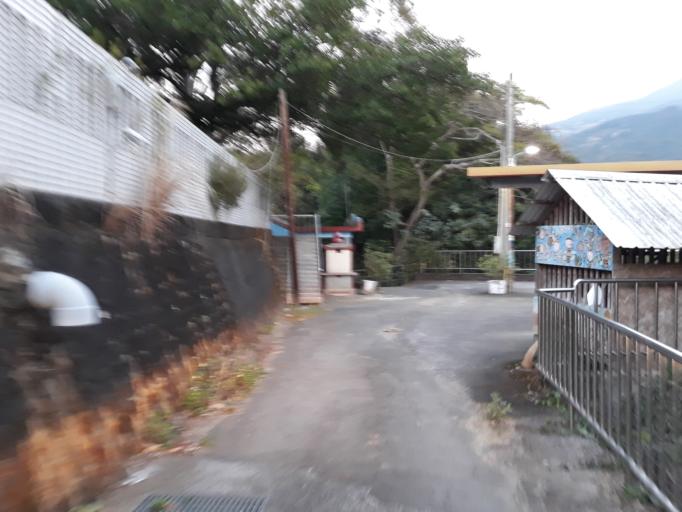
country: TW
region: Taiwan
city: Fengyuan
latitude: 24.3525
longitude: 120.8655
